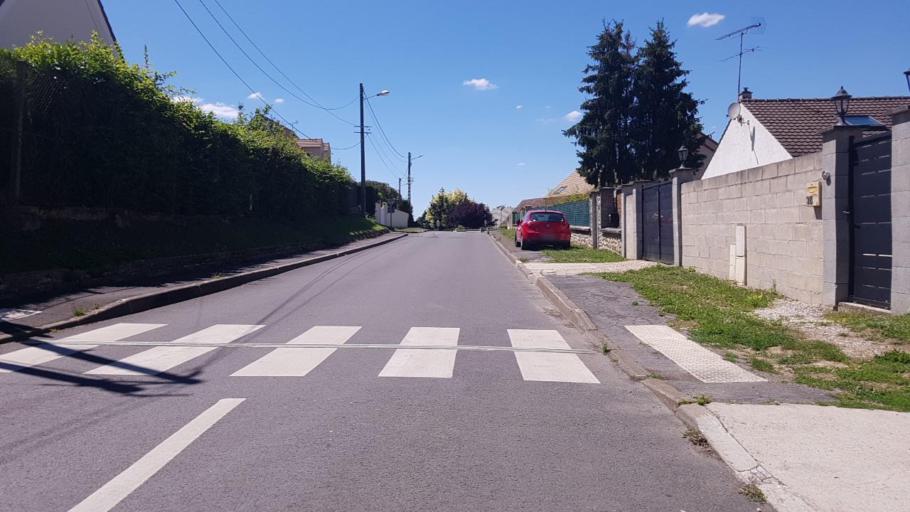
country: FR
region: Ile-de-France
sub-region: Departement de Seine-et-Marne
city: Fublaines
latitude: 48.9393
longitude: 2.9370
